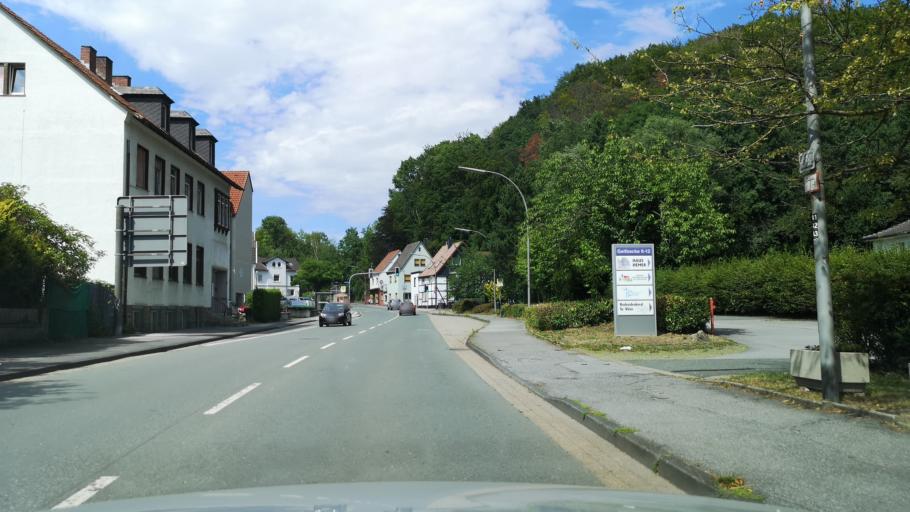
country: DE
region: North Rhine-Westphalia
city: Hemer
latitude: 51.3957
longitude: 7.7600
